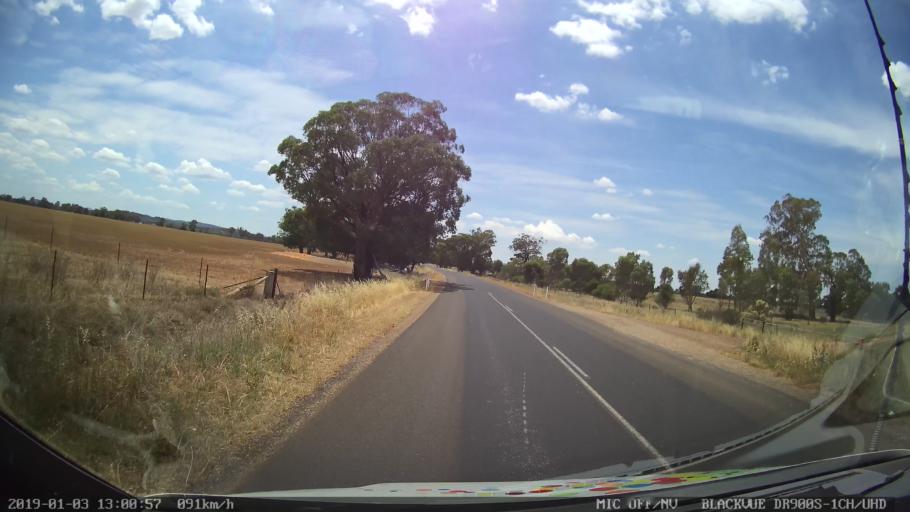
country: AU
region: New South Wales
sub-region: Cabonne
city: Canowindra
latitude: -33.6280
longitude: 148.4114
